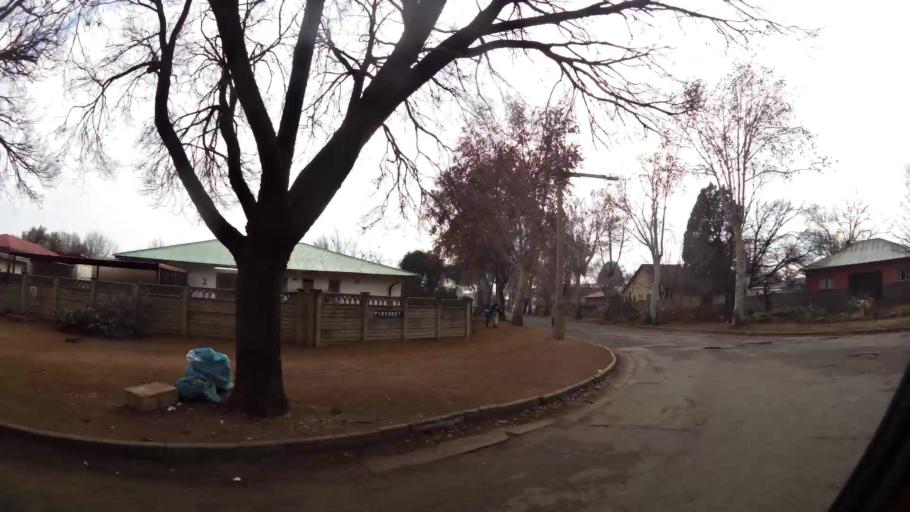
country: ZA
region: Gauteng
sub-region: Sedibeng District Municipality
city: Vanderbijlpark
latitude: -26.6835
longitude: 27.8159
